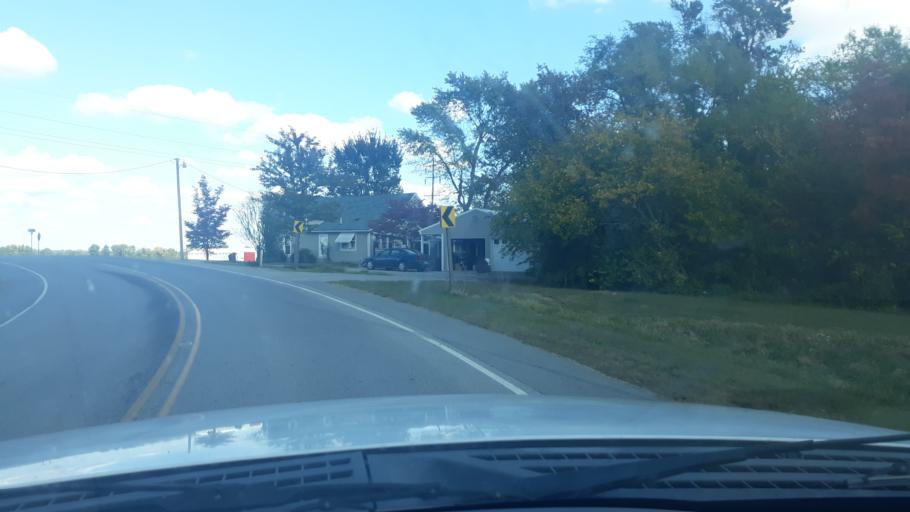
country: US
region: Illinois
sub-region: Saline County
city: Eldorado
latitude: 37.7893
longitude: -88.4852
